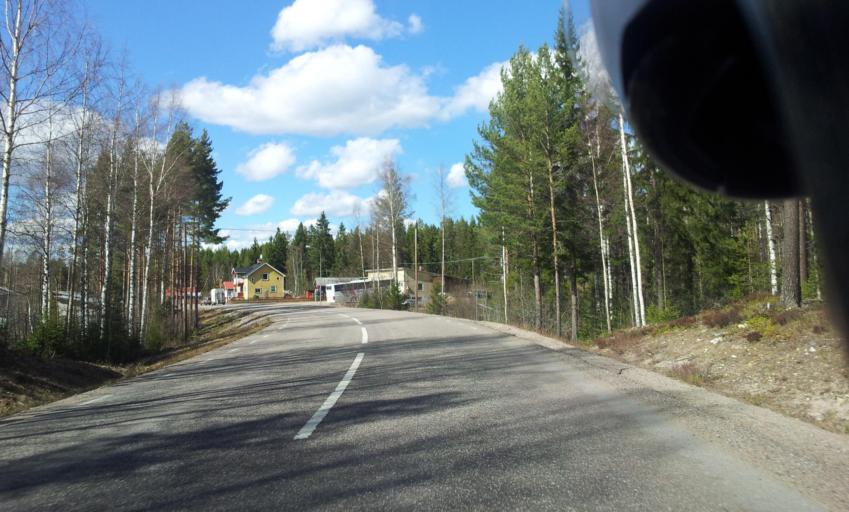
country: SE
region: Gaevleborg
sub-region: Ovanakers Kommun
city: Edsbyn
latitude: 61.2510
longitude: 15.8935
